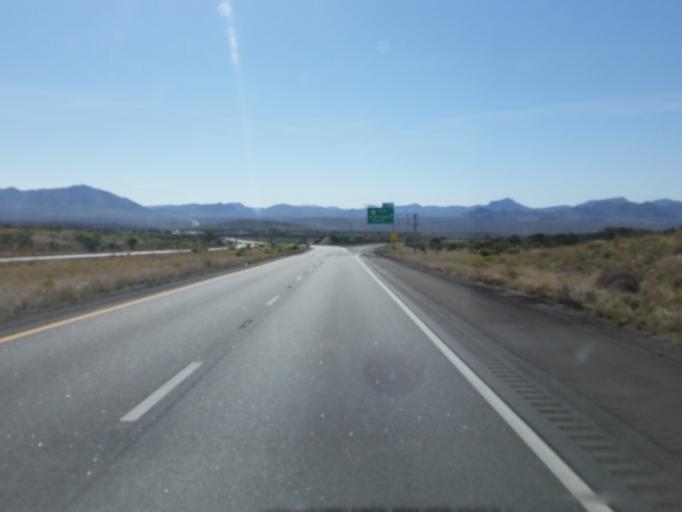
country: US
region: Arizona
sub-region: Mohave County
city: New Kingman-Butler
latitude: 35.1596
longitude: -113.7019
